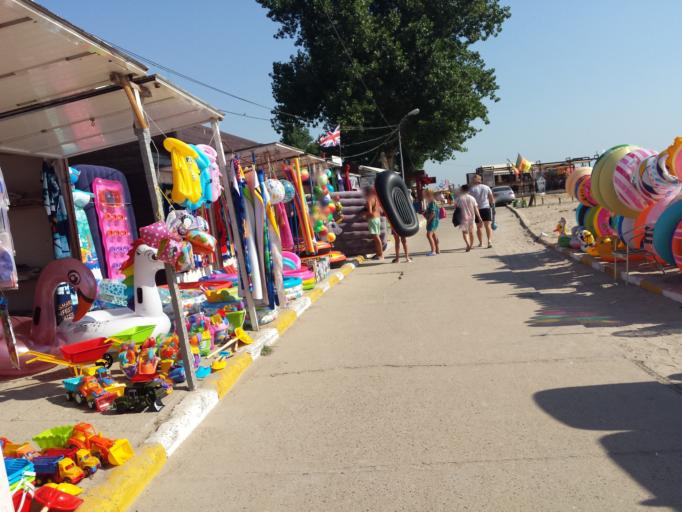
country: RO
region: Constanta
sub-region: Comuna Douazeci si Trei August
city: Douazeci si Trei August
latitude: 43.8595
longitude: 28.6060
